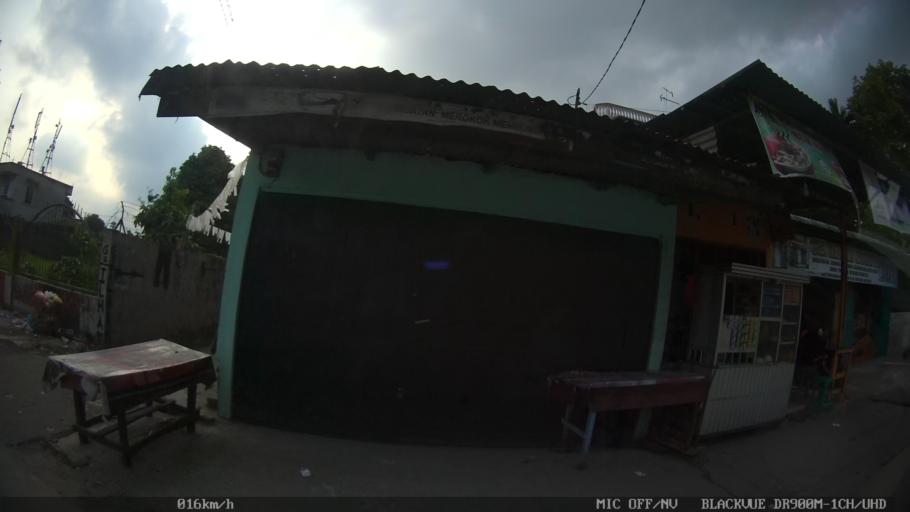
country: ID
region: North Sumatra
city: Medan
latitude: 3.5832
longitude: 98.7313
